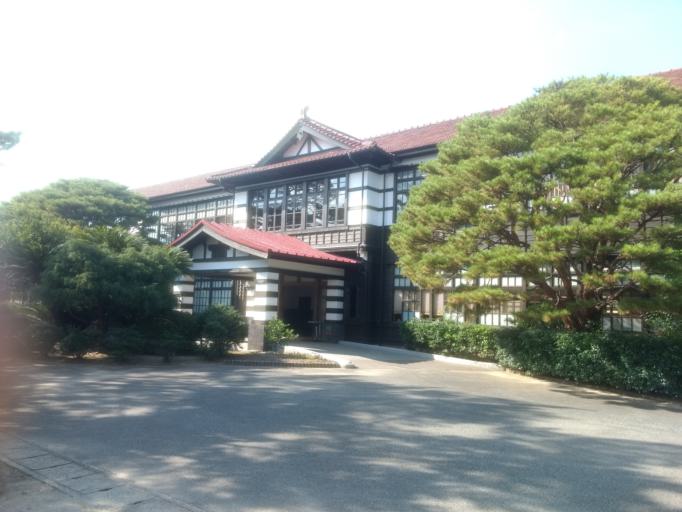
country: JP
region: Yamaguchi
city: Hagi
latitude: 34.4090
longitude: 131.4000
